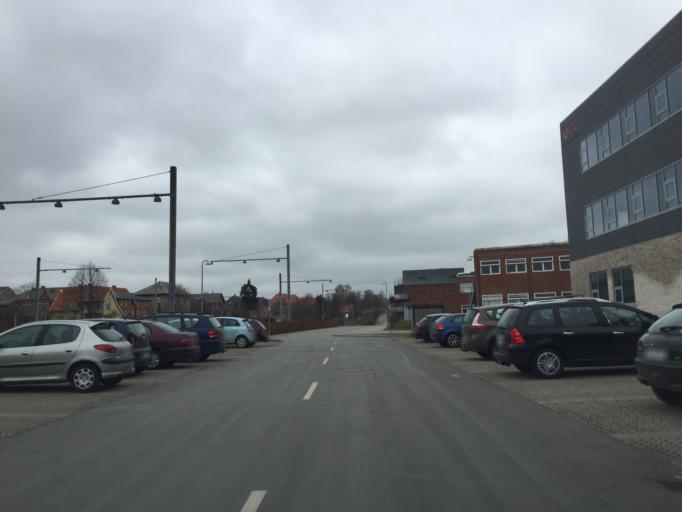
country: DK
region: Capital Region
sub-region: Hillerod Kommune
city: Hillerod
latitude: 55.9298
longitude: 12.3126
